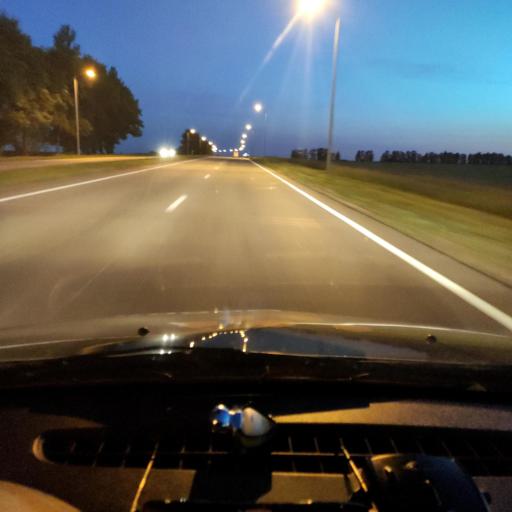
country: RU
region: Belgorod
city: Skorodnoye
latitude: 51.1751
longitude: 37.3308
